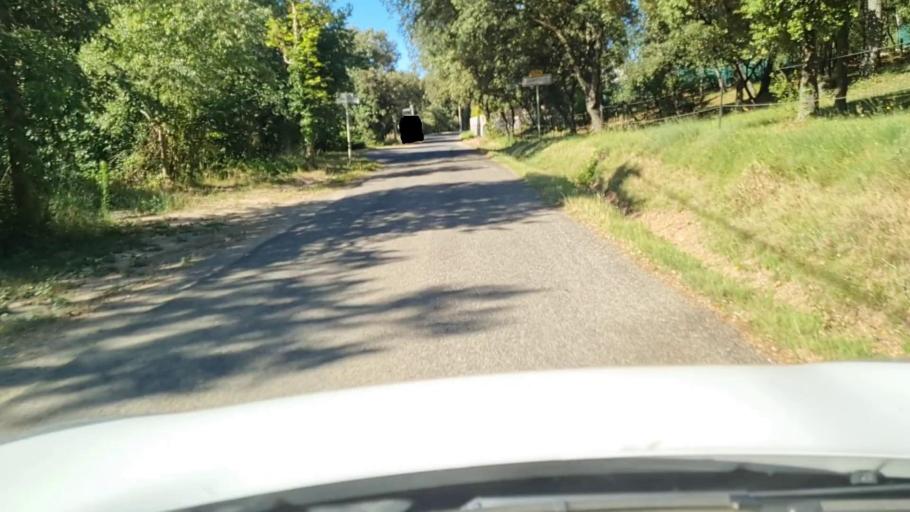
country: FR
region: Languedoc-Roussillon
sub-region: Departement du Gard
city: Sommieres
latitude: 43.8120
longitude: 4.0505
